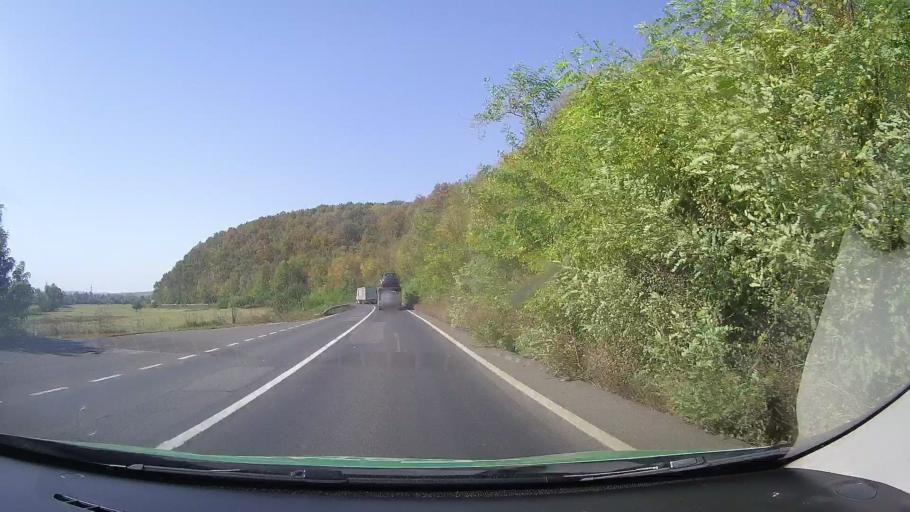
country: RO
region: Arad
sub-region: Comuna Bata
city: Bata
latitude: 46.0371
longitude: 22.0782
